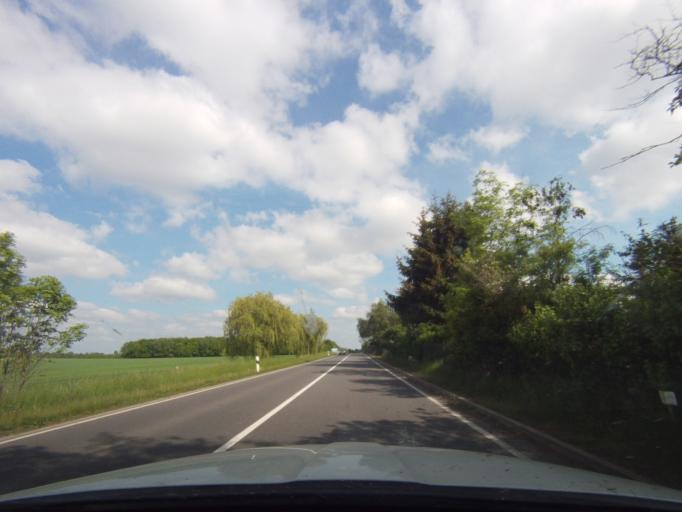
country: DE
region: Thuringia
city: Ronneburg
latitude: 50.8699
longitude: 12.1705
